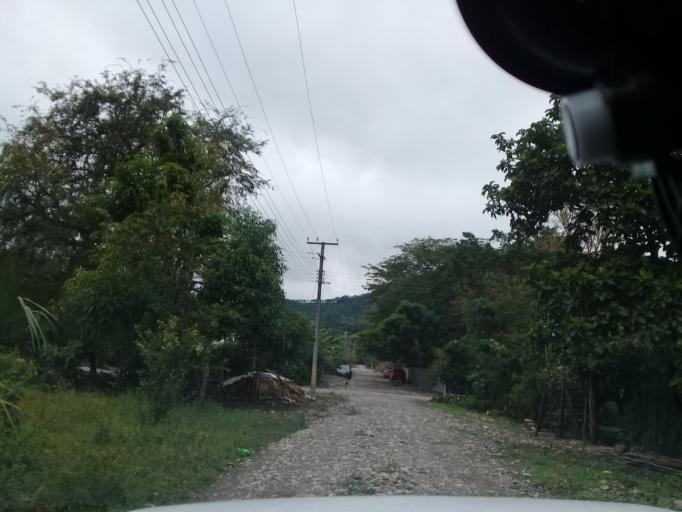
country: MX
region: Veracruz
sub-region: Chalma
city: San Pedro Coyutla
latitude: 21.2220
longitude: -98.4290
